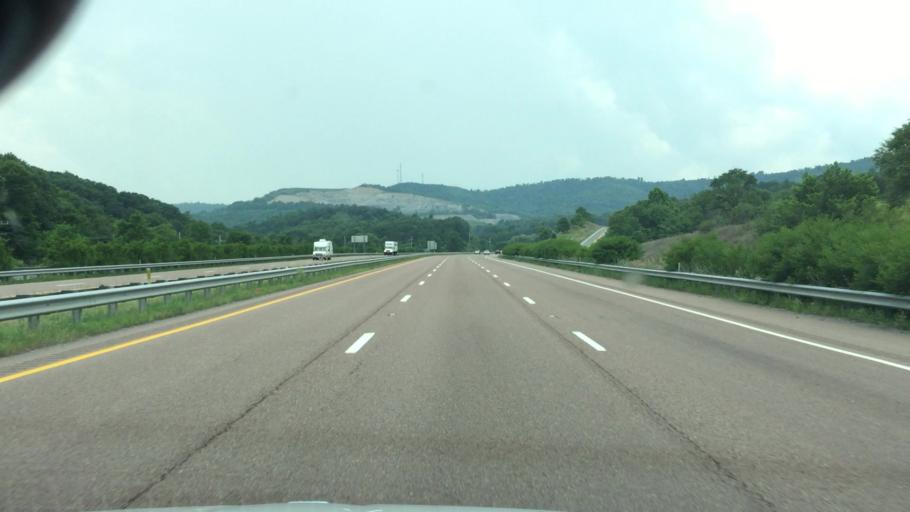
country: US
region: Maryland
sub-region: Allegany County
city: Cumberland
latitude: 39.7072
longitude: -78.5919
